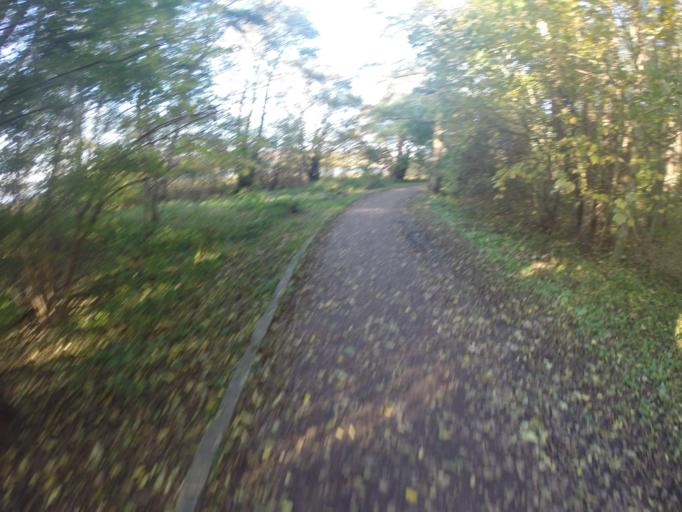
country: DK
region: Capital Region
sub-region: Gladsaxe Municipality
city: Buddinge
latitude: 55.7703
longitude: 12.4682
